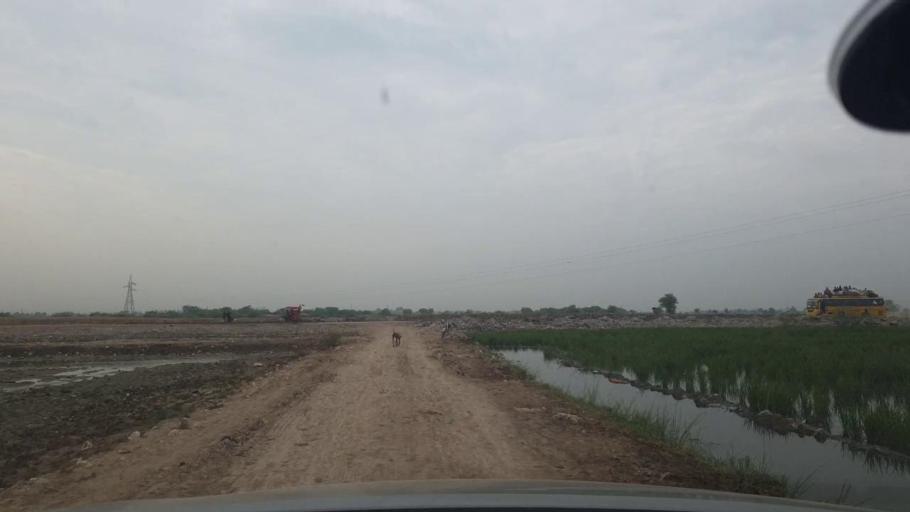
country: PK
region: Sindh
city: Jacobabad
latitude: 28.2858
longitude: 68.4167
